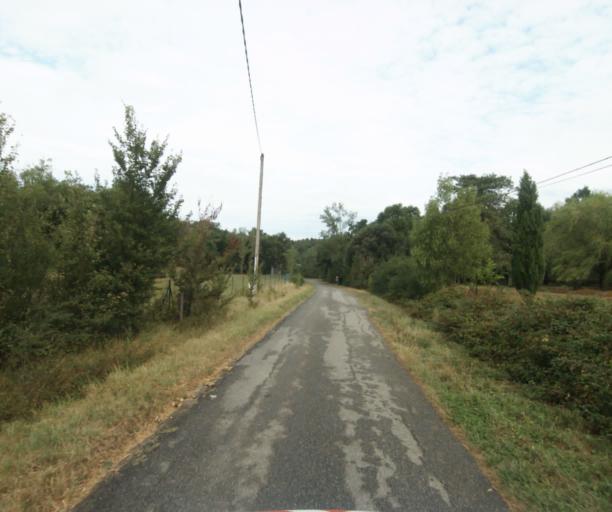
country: FR
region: Midi-Pyrenees
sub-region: Departement de la Haute-Garonne
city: Revel
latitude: 43.4274
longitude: 1.9957
